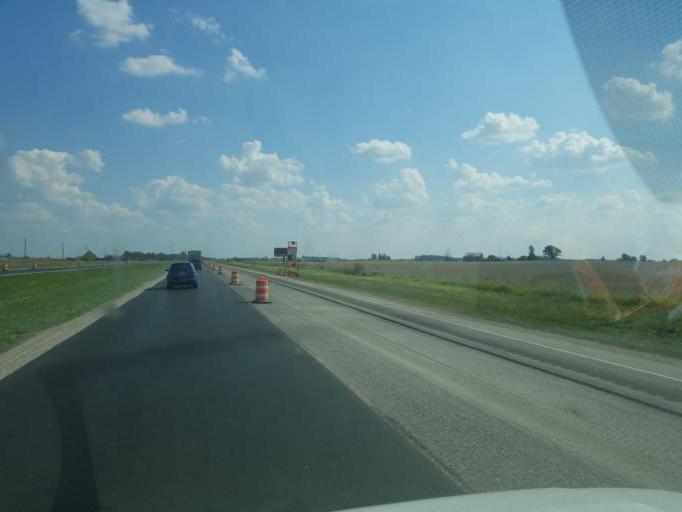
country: US
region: Ohio
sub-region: Van Wert County
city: Convoy
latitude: 40.9515
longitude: -84.7239
